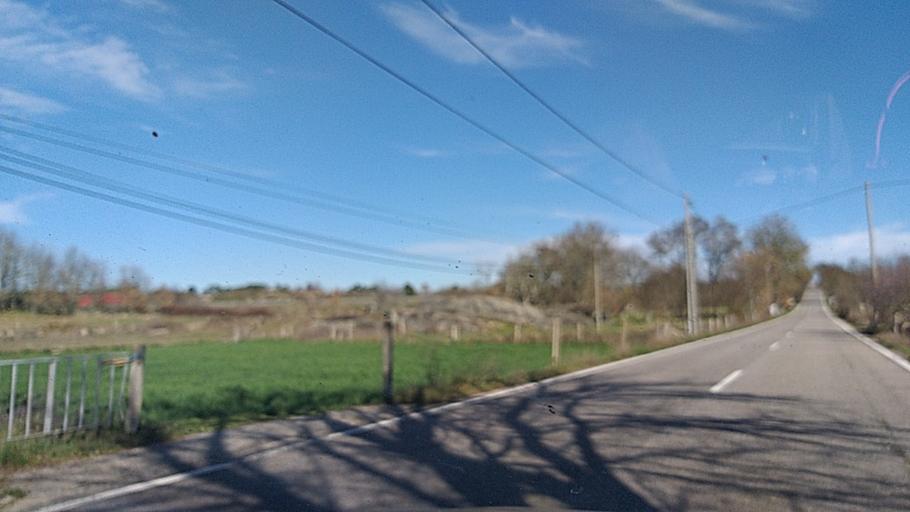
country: PT
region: Guarda
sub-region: Guarda
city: Sequeira
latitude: 40.6005
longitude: -7.1012
